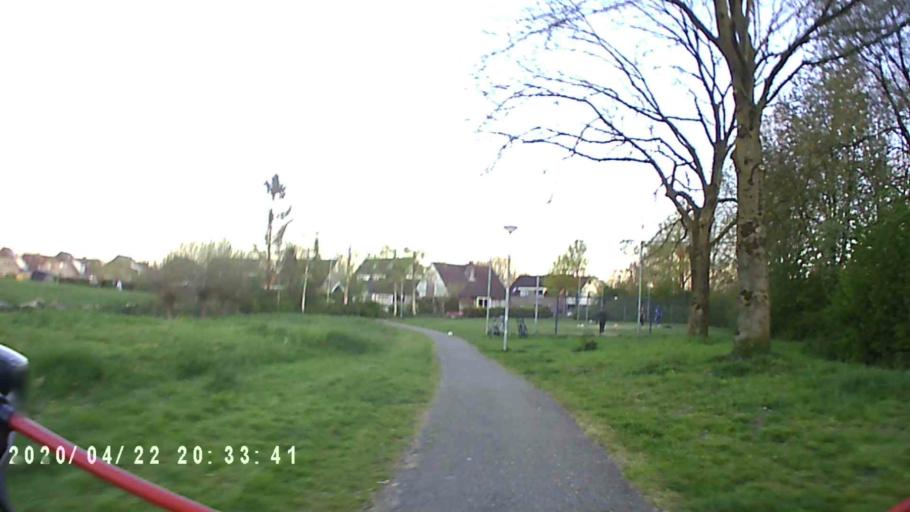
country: NL
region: Groningen
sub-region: Gemeente Winsum
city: Winsum
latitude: 53.3258
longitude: 6.5230
